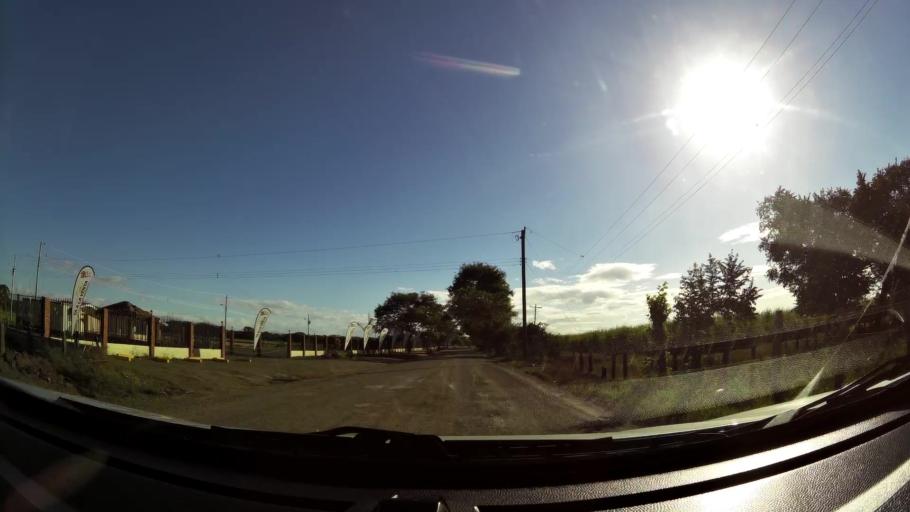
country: CR
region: Guanacaste
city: Sardinal
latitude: 10.4856
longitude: -85.5787
